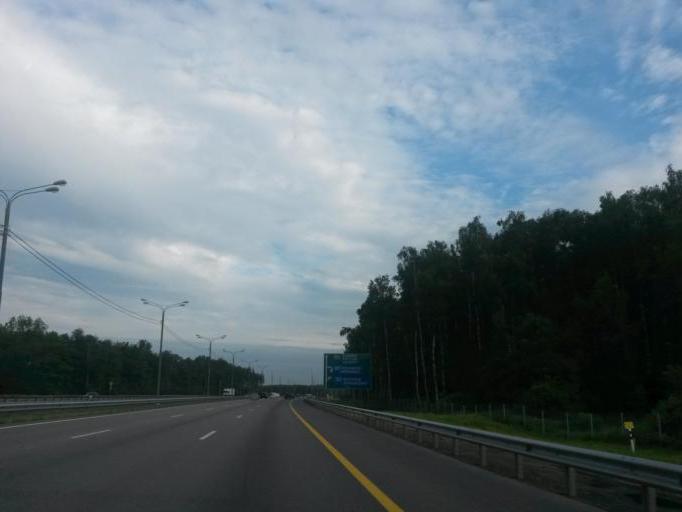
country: RU
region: Moskovskaya
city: Vostryakovo
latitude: 55.3521
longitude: 37.8043
